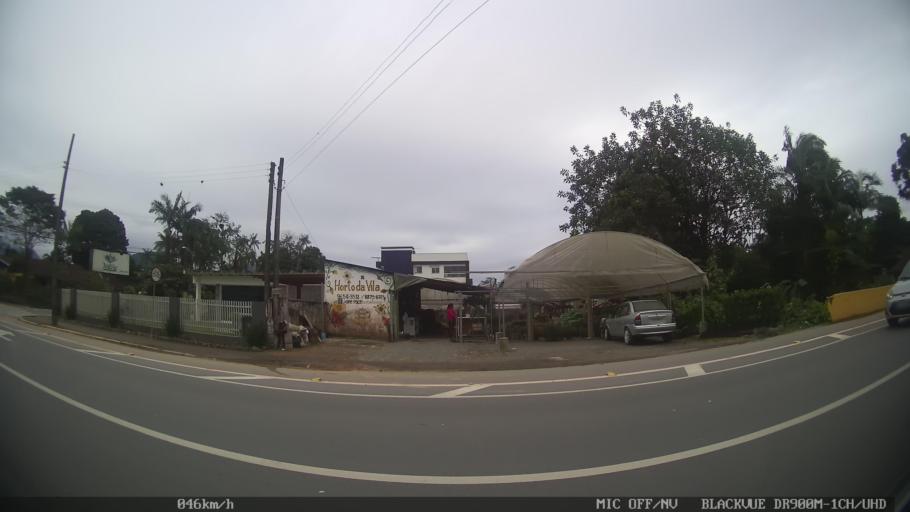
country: BR
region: Santa Catarina
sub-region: Joinville
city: Joinville
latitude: -26.2872
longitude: -48.9159
